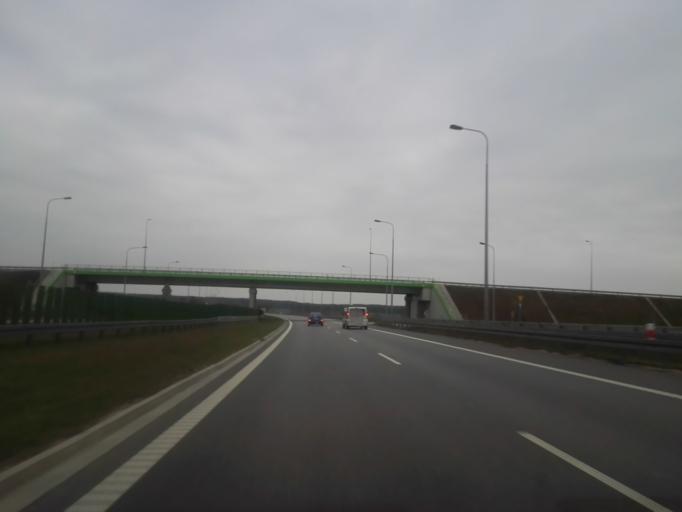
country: PL
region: Podlasie
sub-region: Powiat kolnenski
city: Stawiski
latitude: 53.3875
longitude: 22.1448
